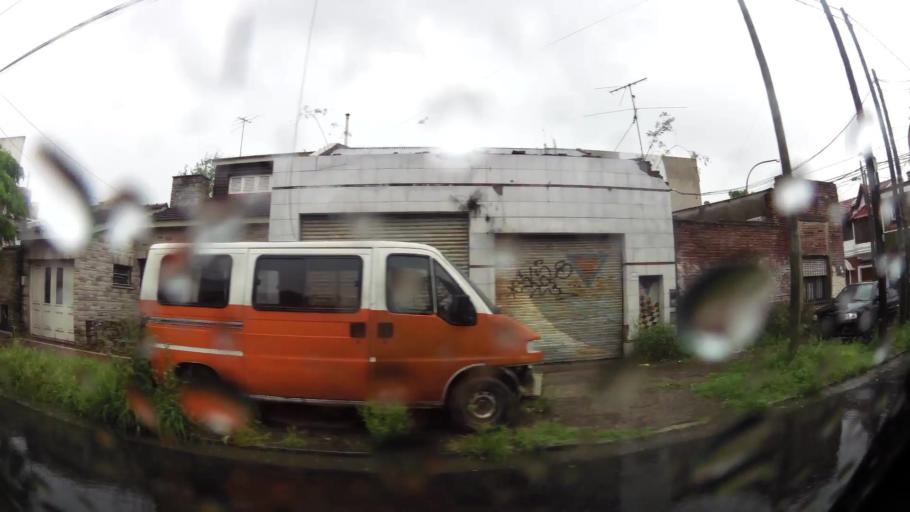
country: AR
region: Buenos Aires
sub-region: Partido de Lanus
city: Lanus
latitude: -34.7263
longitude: -58.4012
